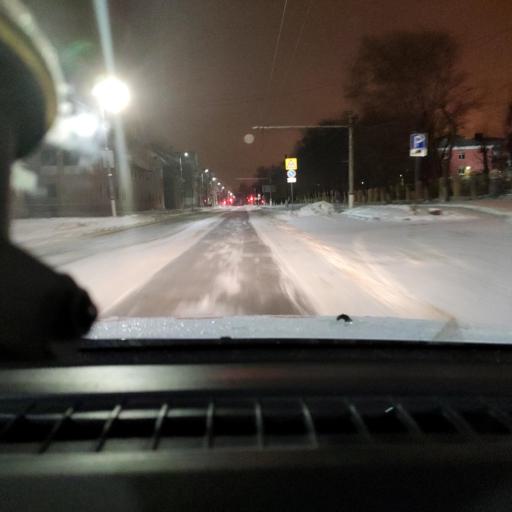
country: RU
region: Samara
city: Novokuybyshevsk
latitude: 53.1034
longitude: 49.9464
